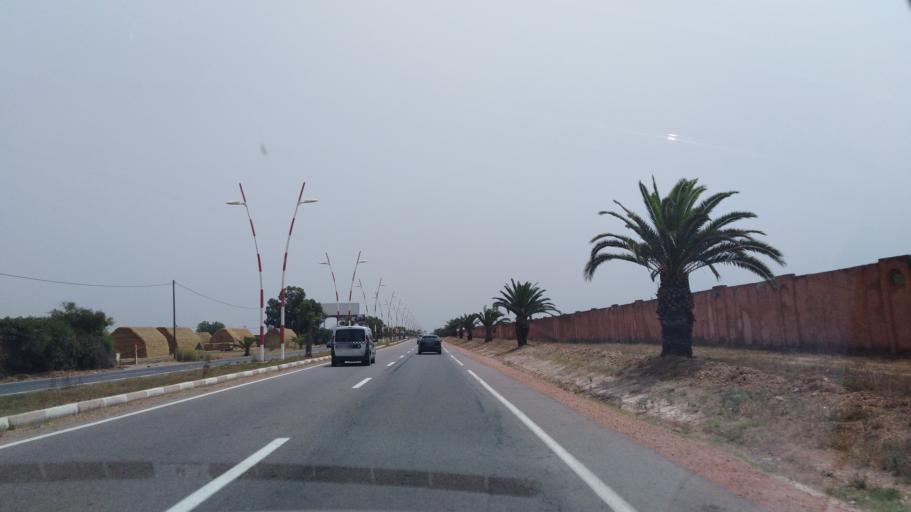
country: MA
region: Chaouia-Ouardigha
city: Nouaseur
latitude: 33.3926
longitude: -7.6019
